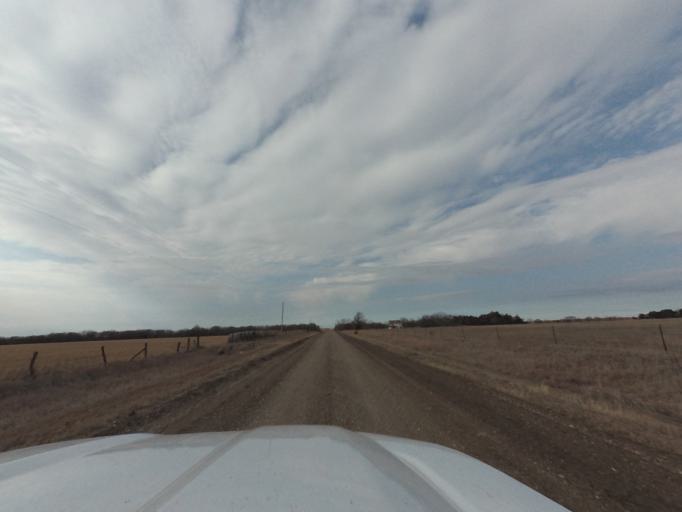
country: US
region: Kansas
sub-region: Chase County
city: Cottonwood Falls
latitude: 38.2170
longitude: -96.6902
